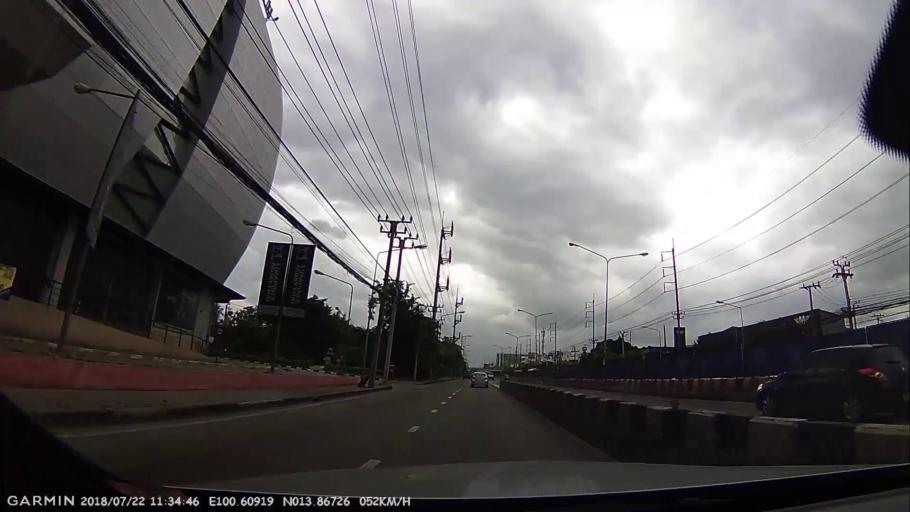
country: TH
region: Bangkok
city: Bang Khen
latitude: 13.8673
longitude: 100.6091
